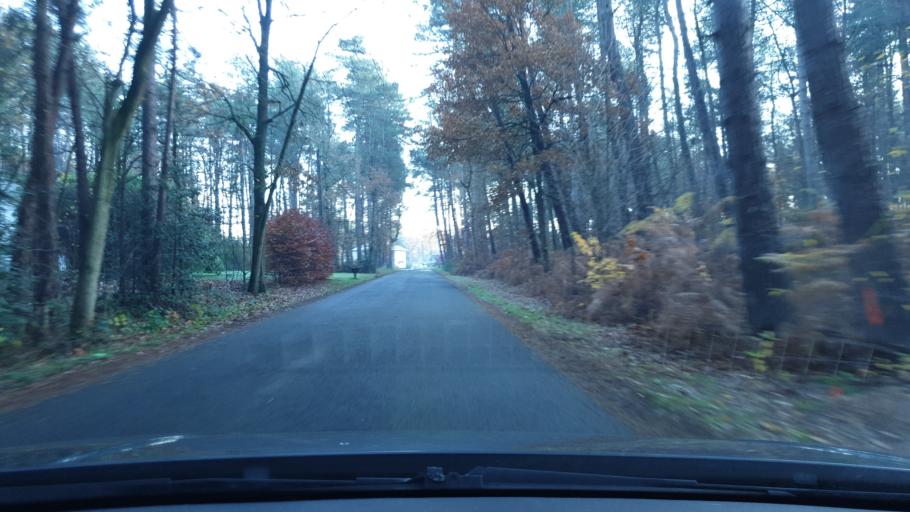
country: BE
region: Flanders
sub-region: Provincie Antwerpen
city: Geel
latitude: 51.1367
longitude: 5.0049
